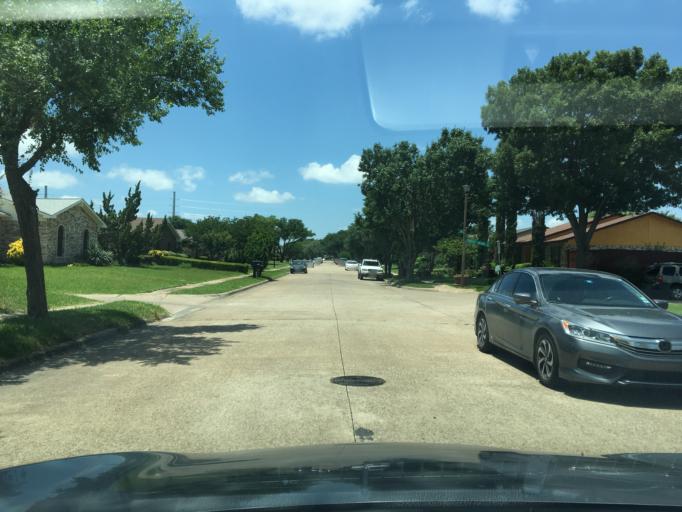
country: US
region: Texas
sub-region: Dallas County
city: Garland
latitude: 32.9523
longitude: -96.6710
